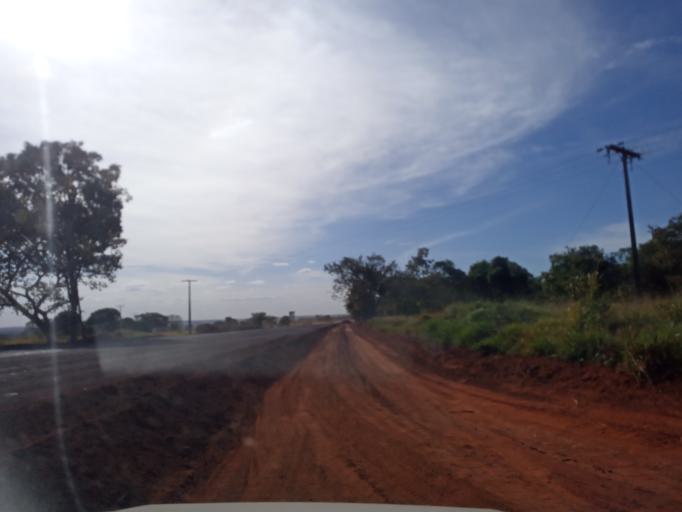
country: BR
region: Minas Gerais
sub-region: Ituiutaba
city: Ituiutaba
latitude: -18.9742
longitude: -49.5049
